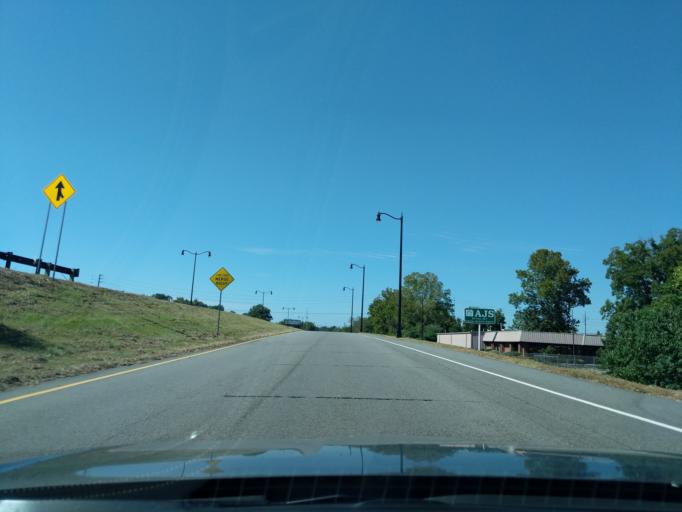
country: US
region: Georgia
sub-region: Richmond County
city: Augusta
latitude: 33.4790
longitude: -81.9863
